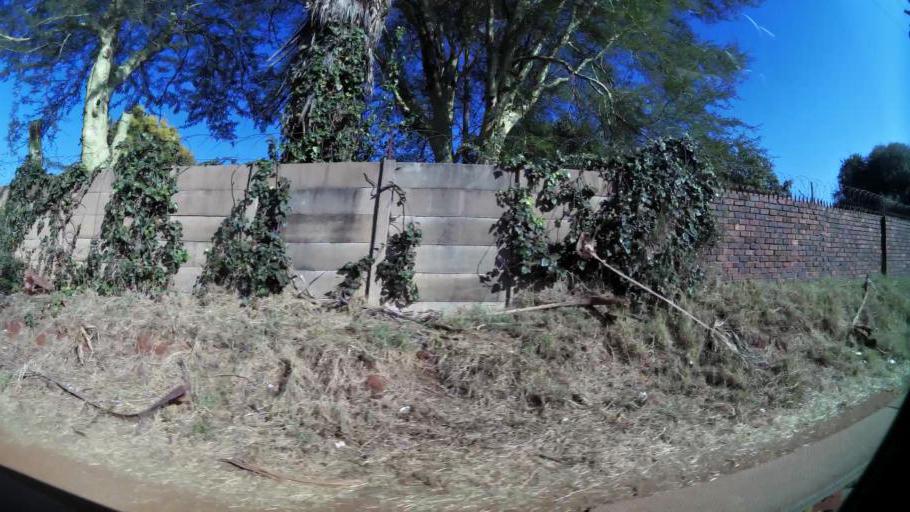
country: ZA
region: Gauteng
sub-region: City of Tshwane Metropolitan Municipality
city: Pretoria
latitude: -25.6596
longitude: 28.1318
